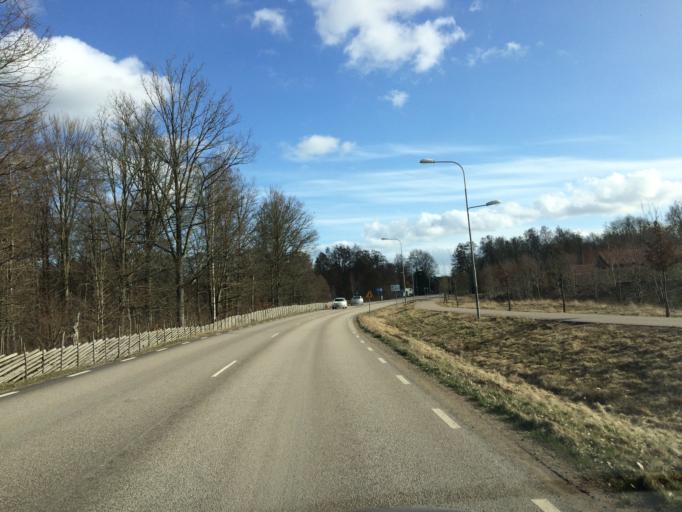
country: SE
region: Kronoberg
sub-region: Almhults Kommun
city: AElmhult
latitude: 56.5639
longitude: 14.1292
